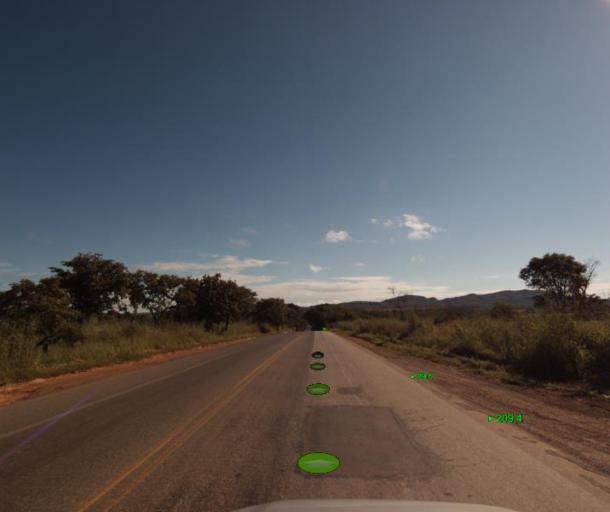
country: BR
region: Goias
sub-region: Uruacu
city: Uruacu
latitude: -14.6076
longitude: -49.1672
